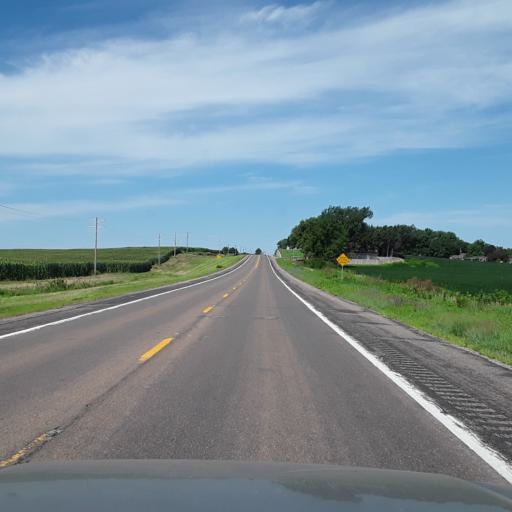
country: US
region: Nebraska
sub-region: Seward County
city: Seward
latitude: 40.9016
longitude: -97.1400
